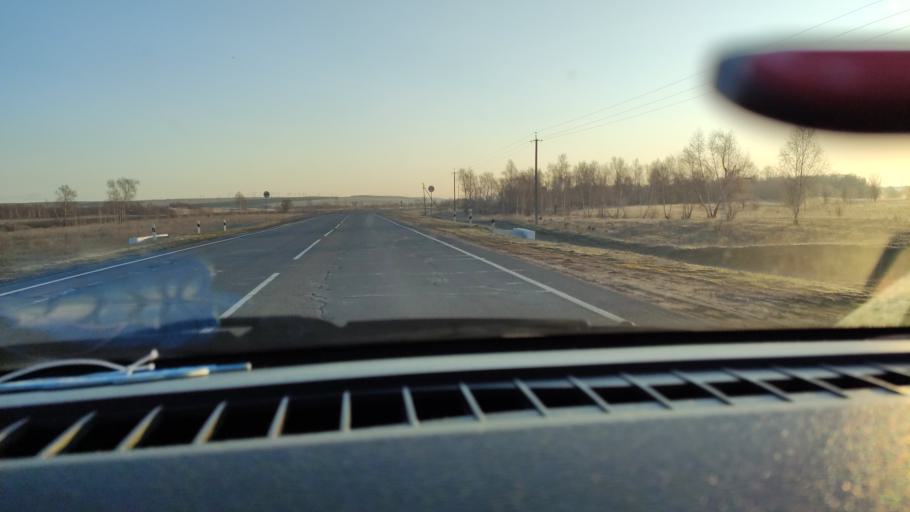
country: RU
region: Saratov
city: Sinodskoye
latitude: 52.0390
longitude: 46.7314
